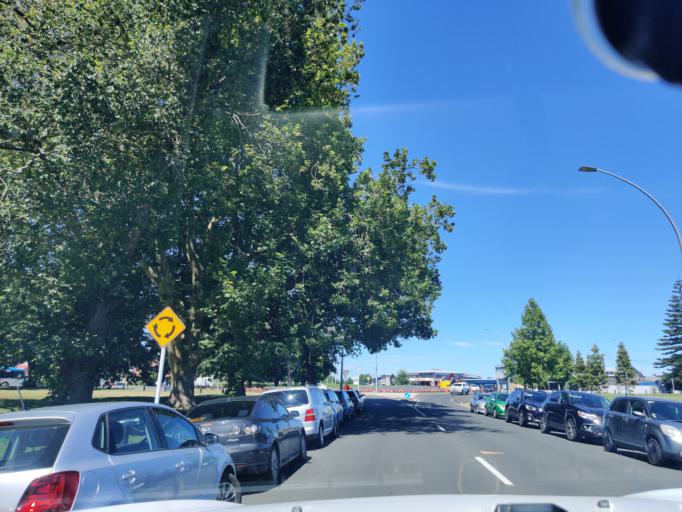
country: NZ
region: Waikato
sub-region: Hamilton City
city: Hamilton
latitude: -37.7845
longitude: 175.2724
